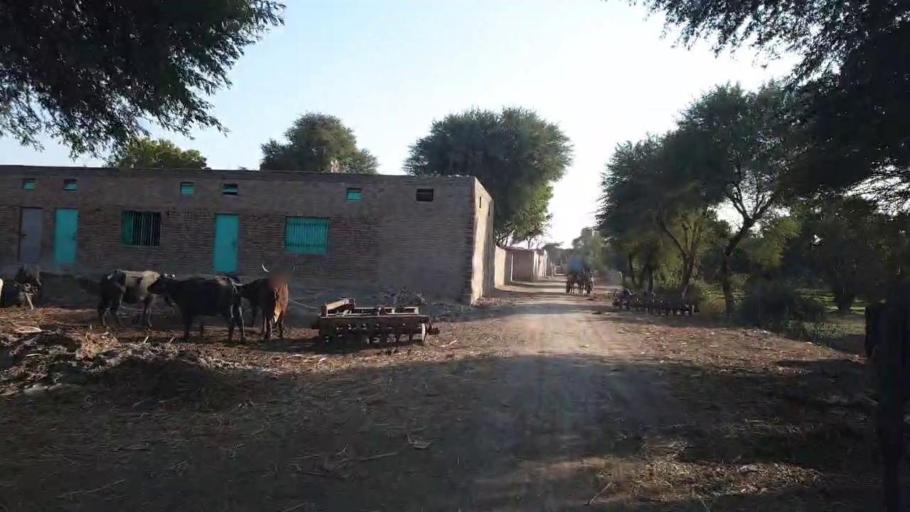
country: PK
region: Sindh
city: Tando Allahyar
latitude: 25.3691
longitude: 68.6798
